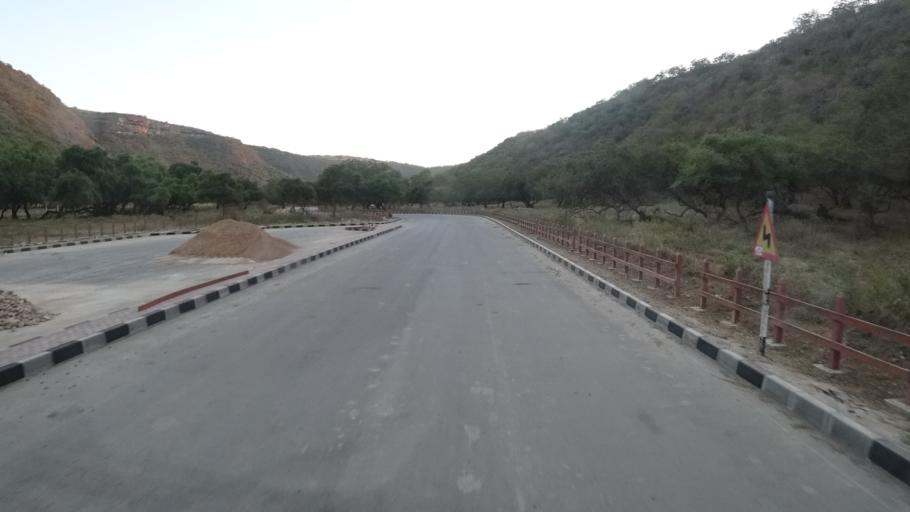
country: OM
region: Zufar
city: Salalah
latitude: 17.1016
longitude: 54.4512
